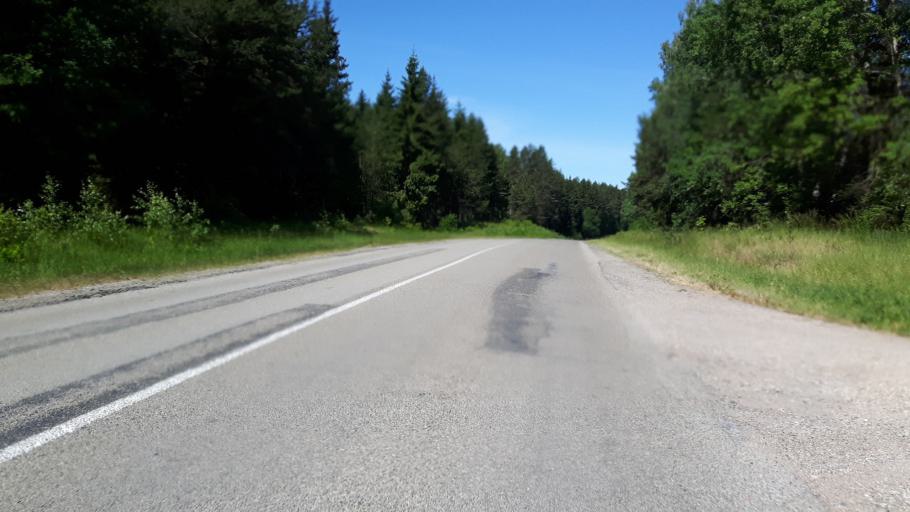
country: LV
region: Tukuma Rajons
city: Tukums
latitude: 57.0056
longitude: 23.0668
